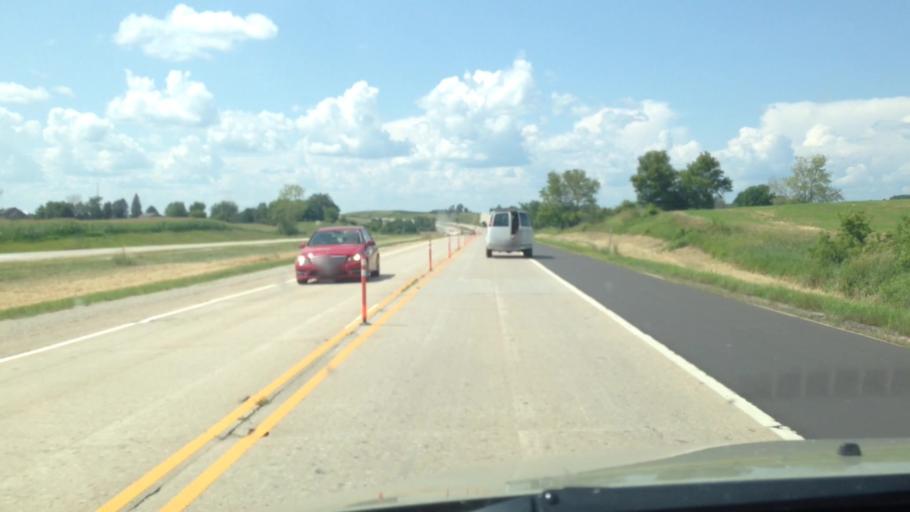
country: US
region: Wisconsin
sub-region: Shawano County
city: Bonduel
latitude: 44.7136
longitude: -88.3876
